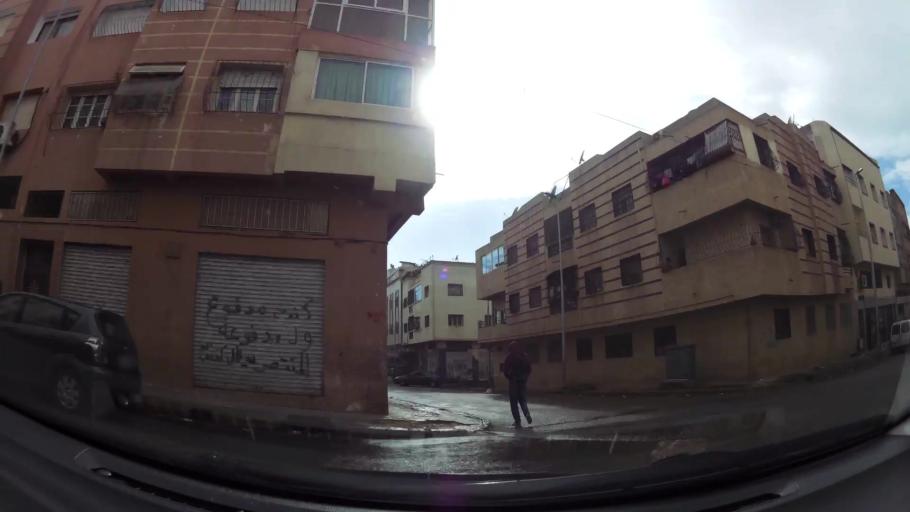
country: MA
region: Grand Casablanca
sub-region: Casablanca
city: Casablanca
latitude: 33.5637
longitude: -7.6928
